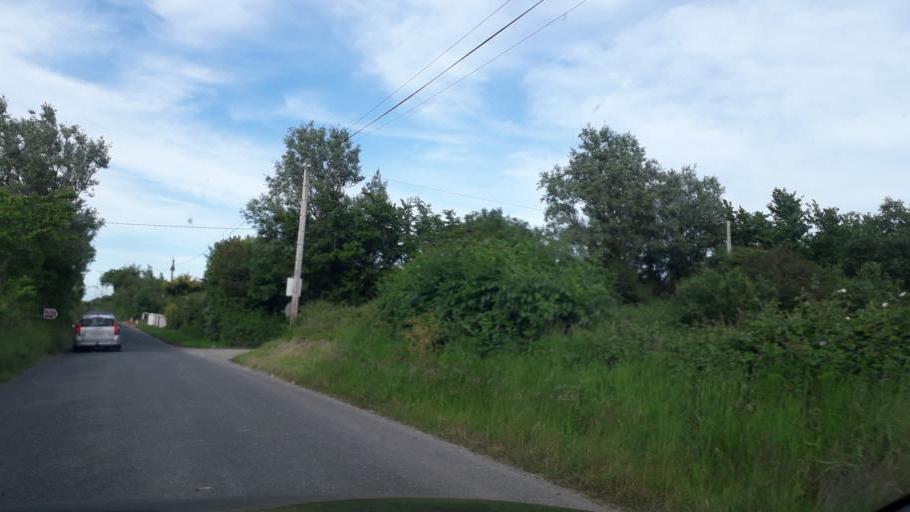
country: IE
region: Leinster
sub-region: Loch Garman
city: Courtown
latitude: 52.5301
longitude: -6.2640
